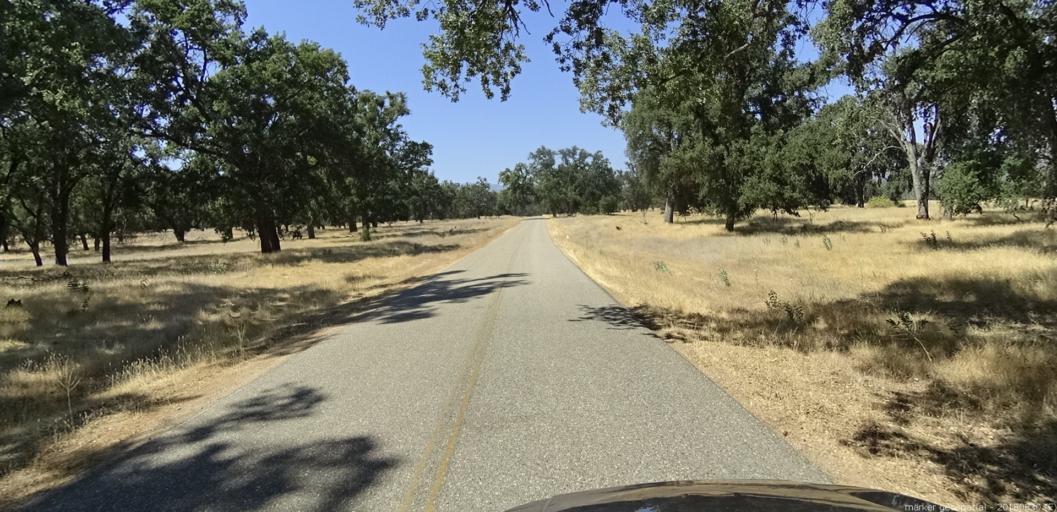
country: US
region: California
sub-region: Monterey County
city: King City
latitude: 36.0489
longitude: -121.3019
